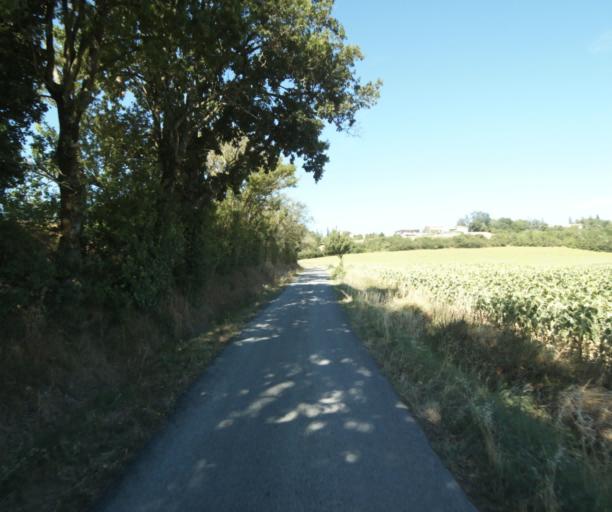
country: FR
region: Midi-Pyrenees
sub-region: Departement de la Haute-Garonne
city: Saint-Felix-Lauragais
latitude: 43.5174
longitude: 1.9129
